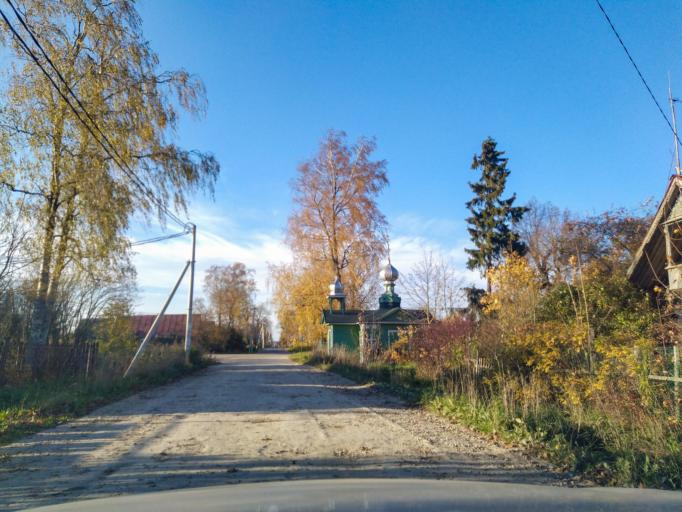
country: RU
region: Leningrad
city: Siverskiy
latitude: 59.3275
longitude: 30.0394
